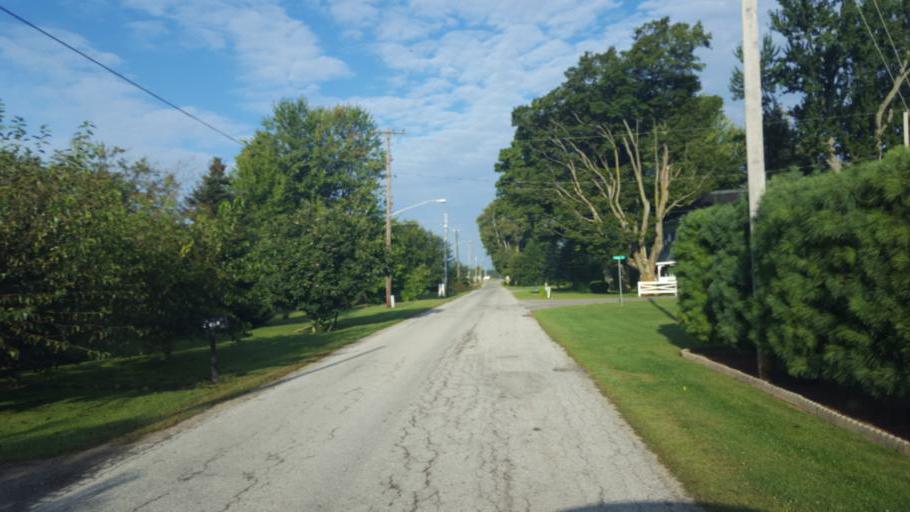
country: US
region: Ohio
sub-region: Morrow County
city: Mount Gilead
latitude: 40.6306
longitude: -82.8874
